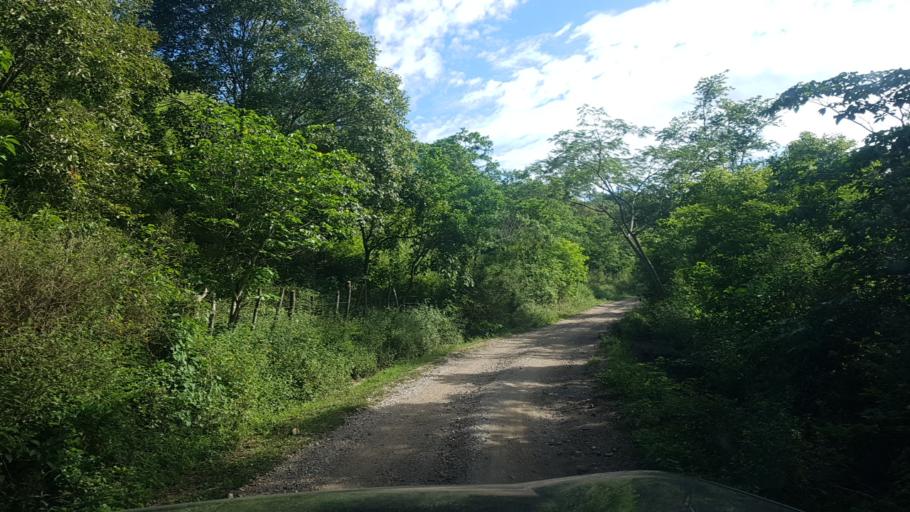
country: NI
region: Nueva Segovia
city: Ocotal
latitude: 13.6067
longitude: -86.4649
